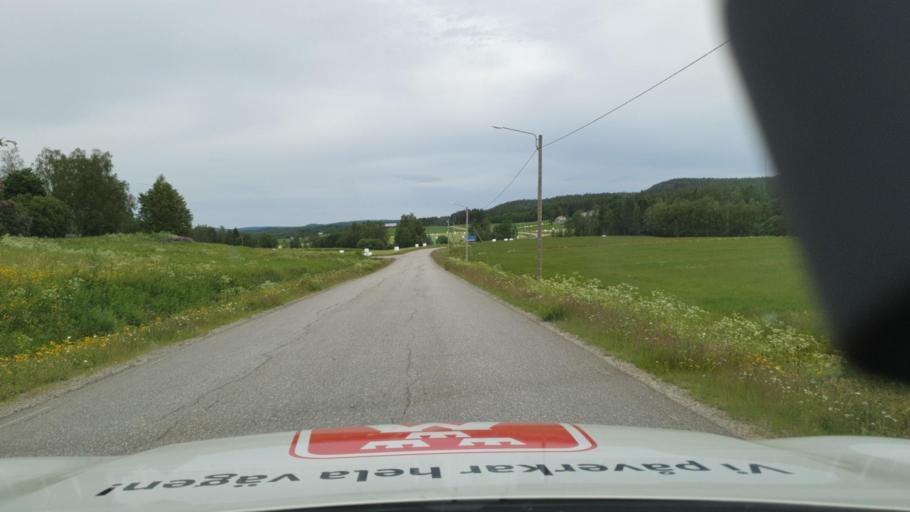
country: SE
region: Vaesterbotten
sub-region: Robertsfors Kommun
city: Robertsfors
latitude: 64.2539
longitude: 20.6566
